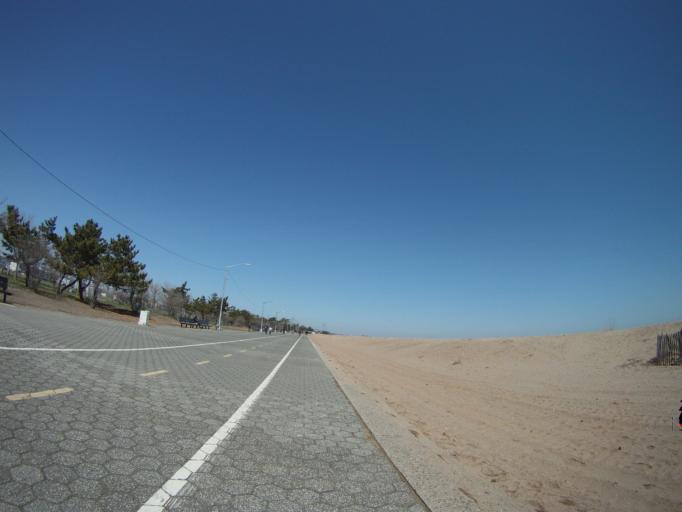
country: US
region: New York
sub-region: Richmond County
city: Staten Island
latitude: 40.5699
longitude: -74.0886
